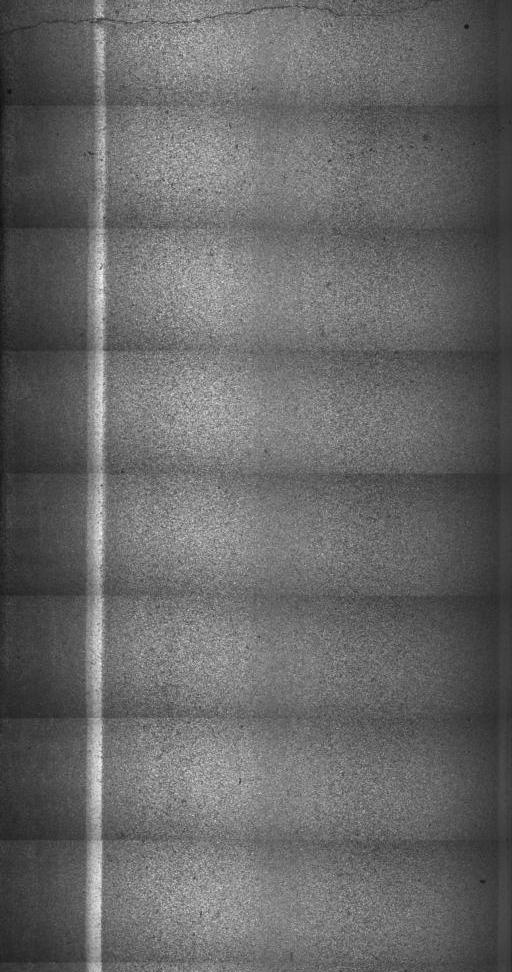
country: US
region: Vermont
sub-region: Windsor County
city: Chester
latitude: 43.2855
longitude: -72.7933
